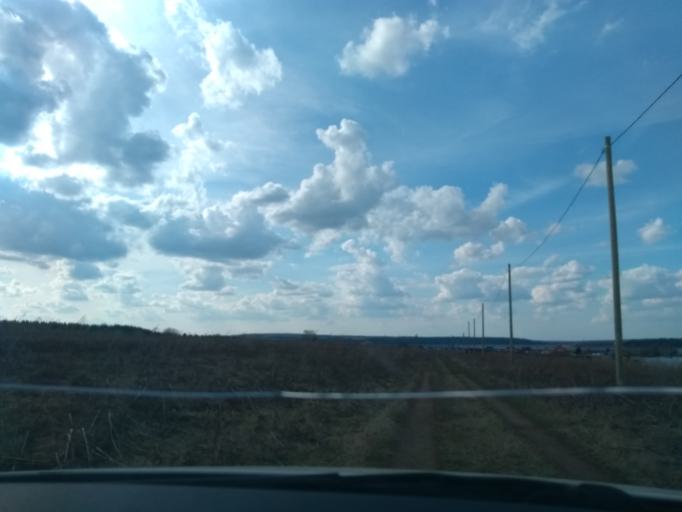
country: RU
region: Perm
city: Sylva
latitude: 57.8439
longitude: 56.7891
